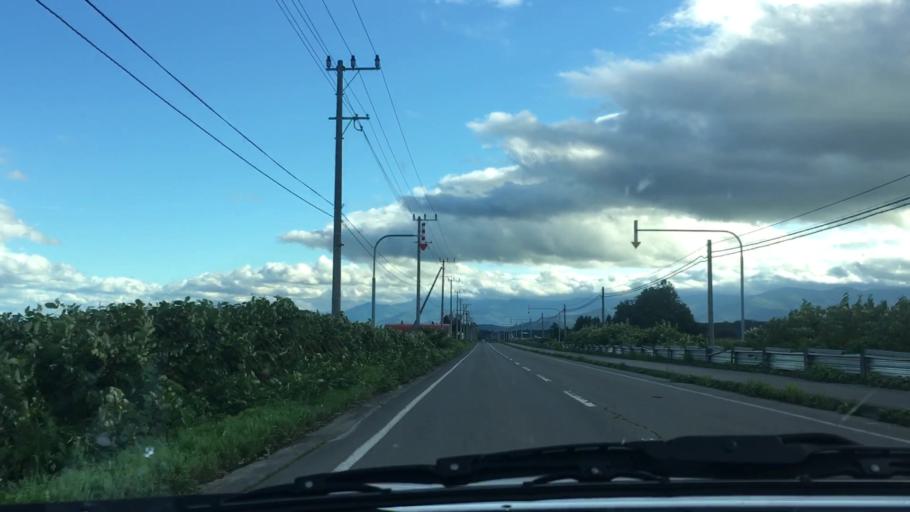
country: JP
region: Hokkaido
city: Otofuke
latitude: 43.1514
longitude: 142.9004
